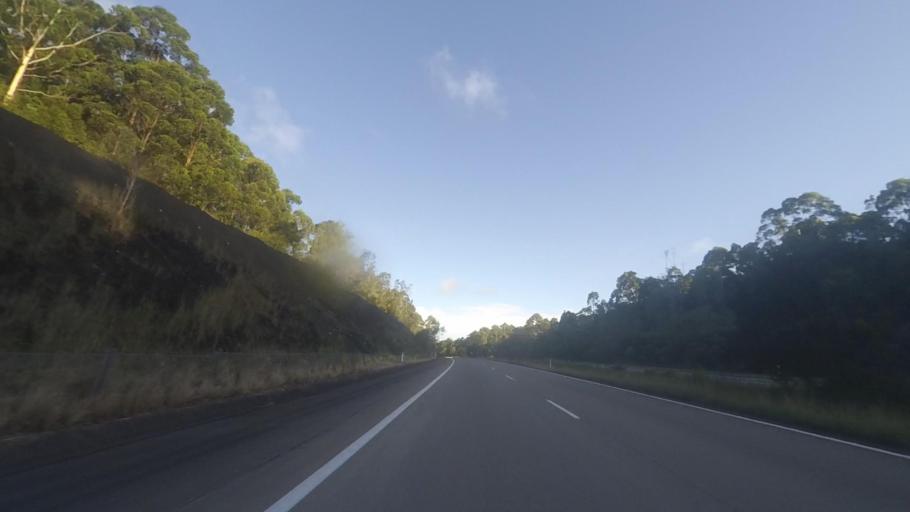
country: AU
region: New South Wales
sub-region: Great Lakes
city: Bulahdelah
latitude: -32.2778
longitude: 152.3309
